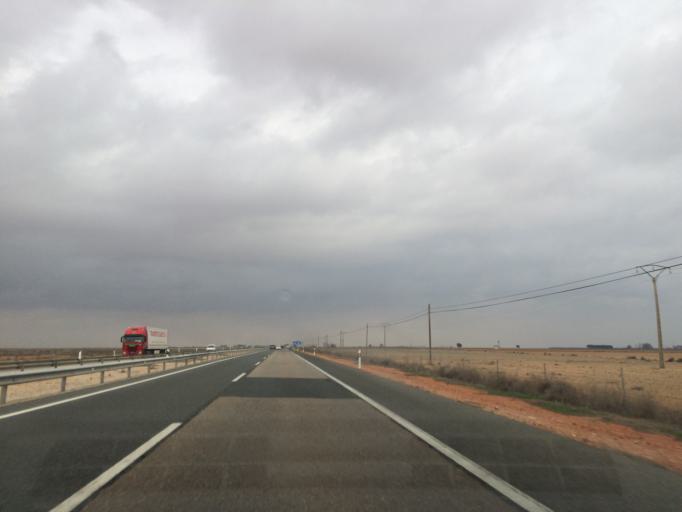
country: ES
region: Castille-La Mancha
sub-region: Province of Toledo
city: Tembleque
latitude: 39.6237
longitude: -3.5210
